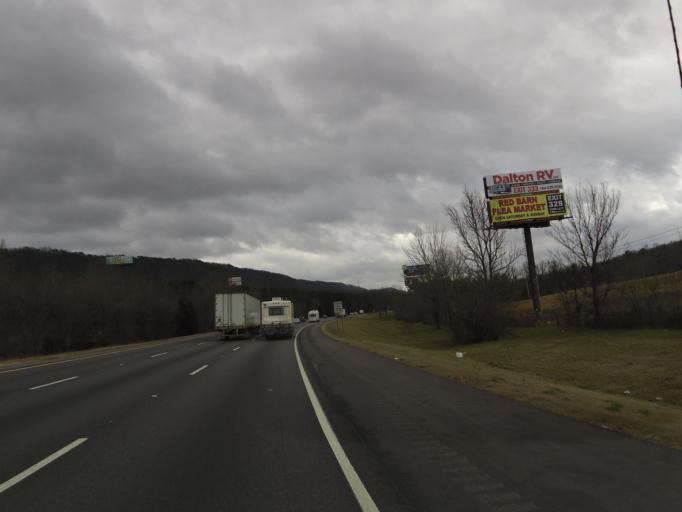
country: US
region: Georgia
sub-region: Whitfield County
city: Varnell
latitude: 34.8557
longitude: -85.0192
